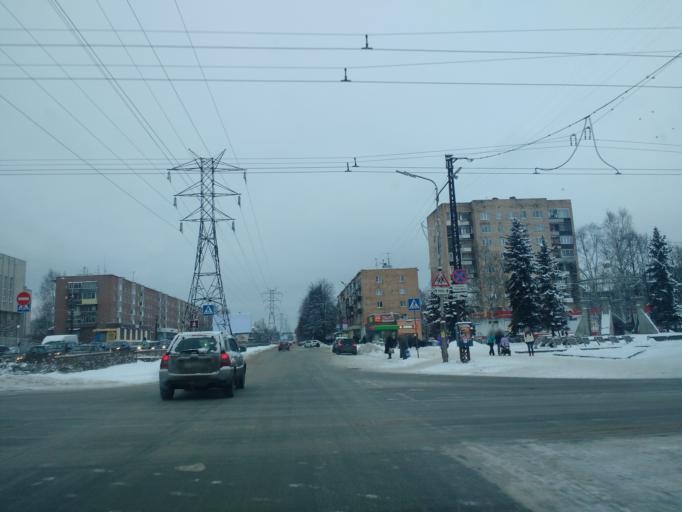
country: RU
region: Republic of Karelia
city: Petrozavodsk
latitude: 61.8002
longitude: 34.3444
